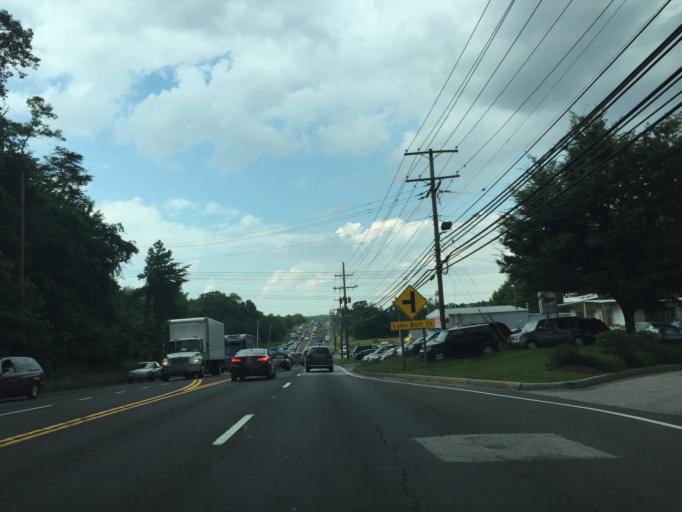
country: US
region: Maryland
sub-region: Howard County
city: Savage
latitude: 39.1215
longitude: -76.8264
